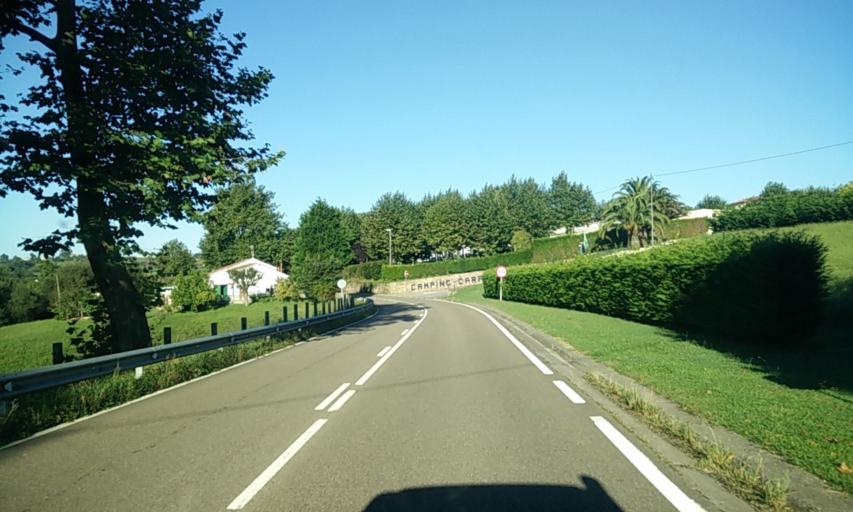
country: ES
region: Cantabria
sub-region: Provincia de Cantabria
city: Comillas
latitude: 43.3842
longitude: -4.3370
